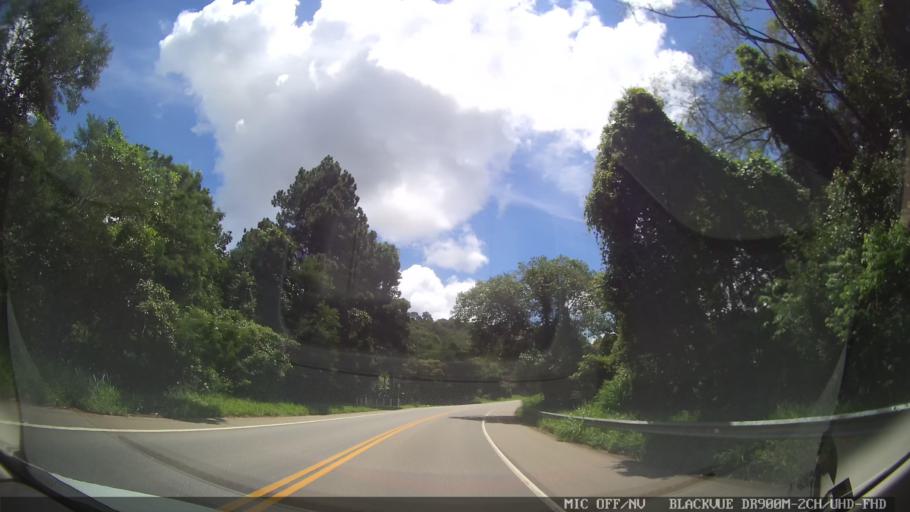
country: BR
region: Sao Paulo
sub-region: Amparo
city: Amparo
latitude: -22.8029
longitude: -46.7177
